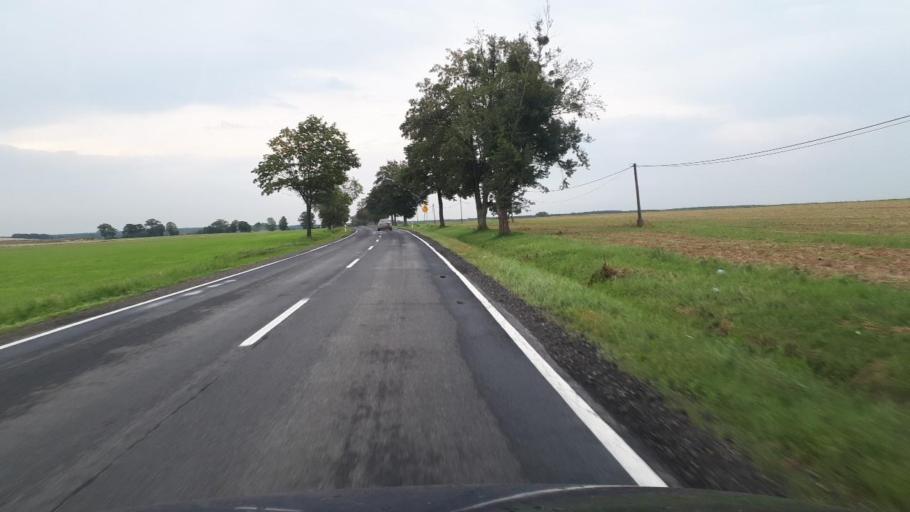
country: PL
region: Silesian Voivodeship
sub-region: Powiat lubliniecki
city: Sierakow Slaski
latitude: 50.8364
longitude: 18.5105
